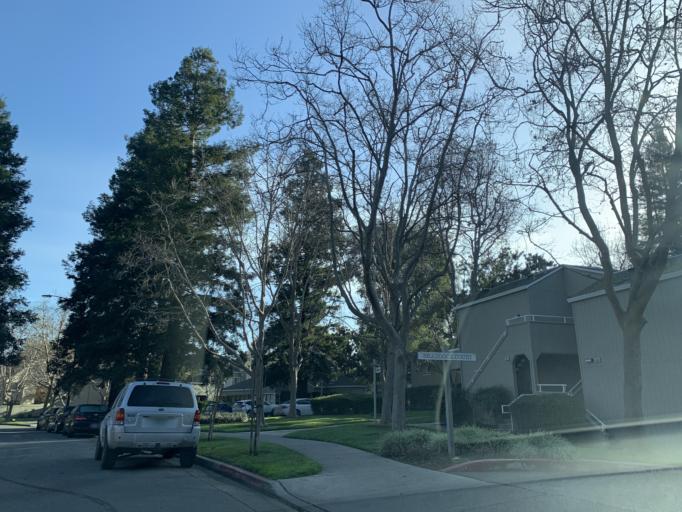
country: US
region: California
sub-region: Santa Clara County
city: Campbell
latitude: 37.2960
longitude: -121.9250
